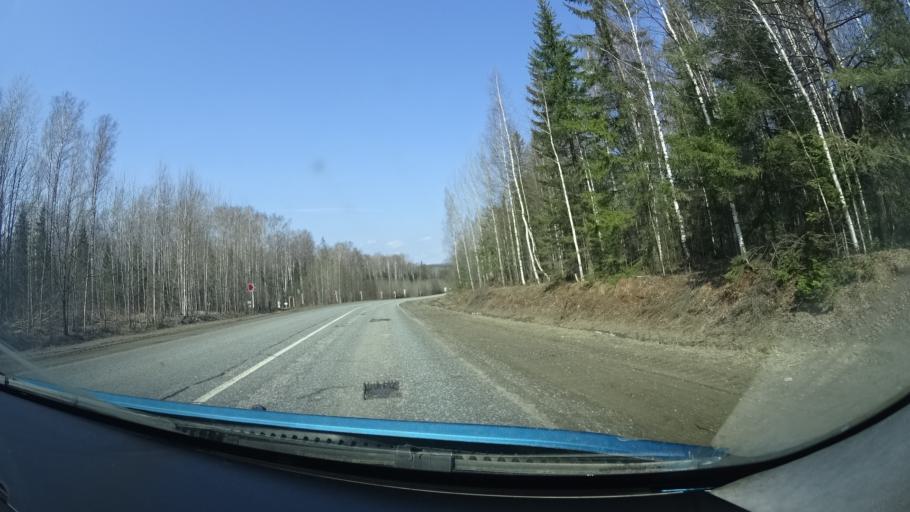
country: RU
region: Perm
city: Yugo-Kamskiy
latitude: 57.5178
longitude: 55.6865
